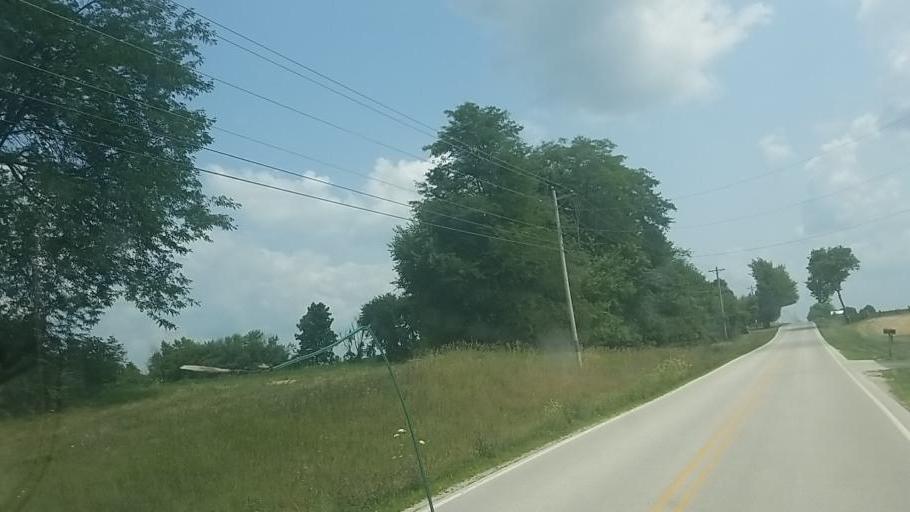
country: US
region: Ohio
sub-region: Wyandot County
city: Carey
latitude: 40.9635
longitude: -83.3306
